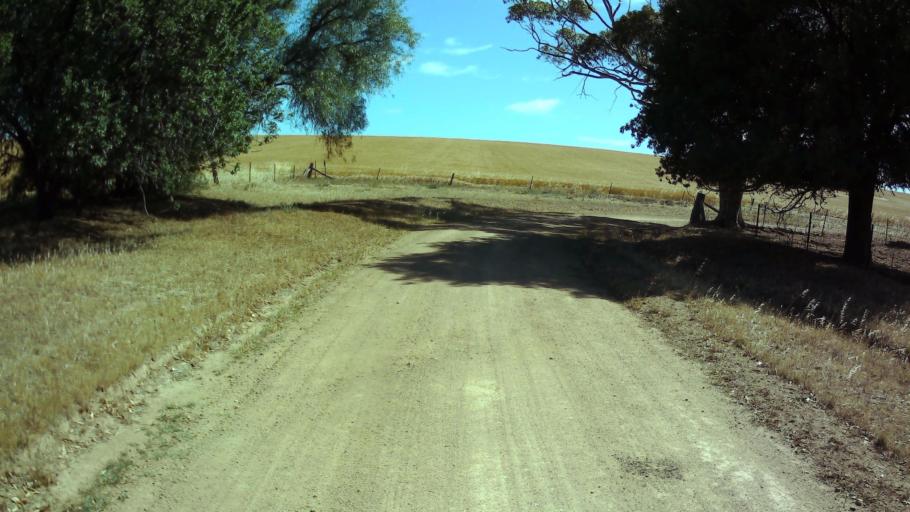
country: AU
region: New South Wales
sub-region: Weddin
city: Grenfell
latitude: -33.9650
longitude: 148.4110
